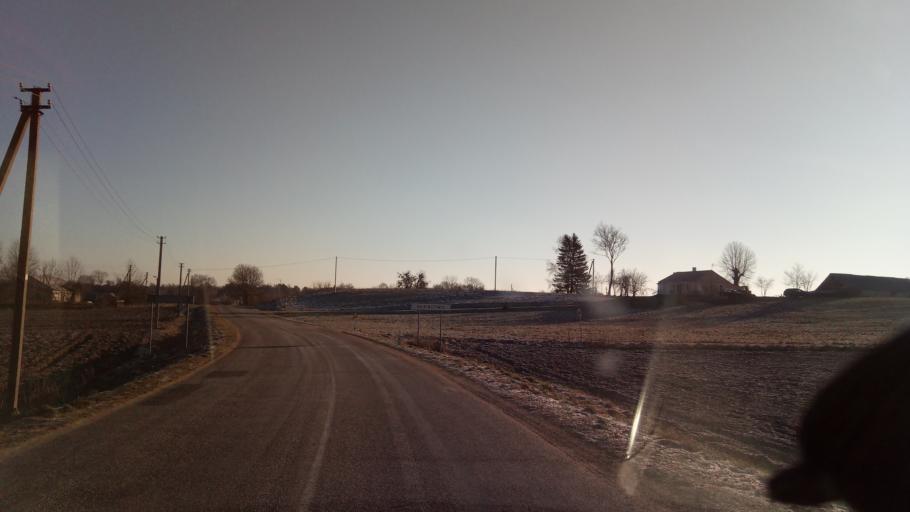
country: LT
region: Alytaus apskritis
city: Druskininkai
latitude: 54.1136
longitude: 24.0130
